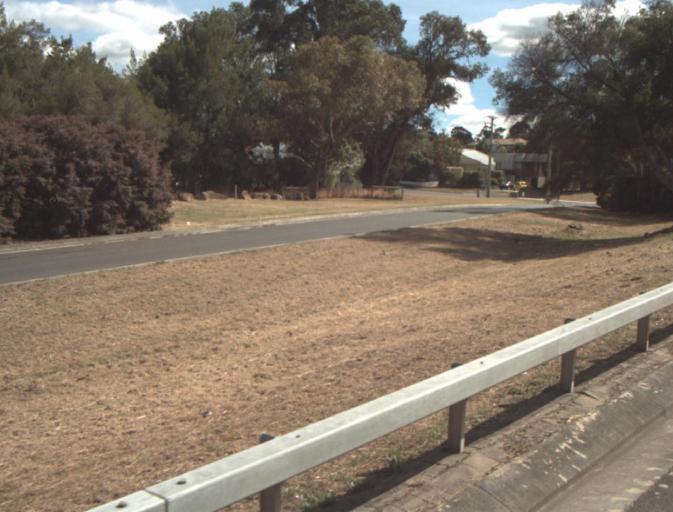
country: AU
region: Tasmania
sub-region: Launceston
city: Newnham
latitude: -41.3954
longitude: 147.1240
